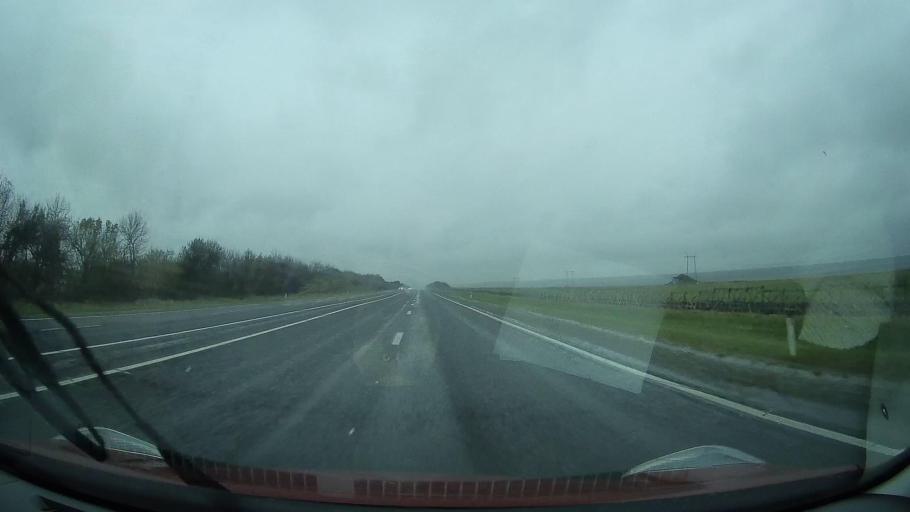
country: RU
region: Stavropol'skiy
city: Nevinnomyssk
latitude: 44.6136
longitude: 42.1135
